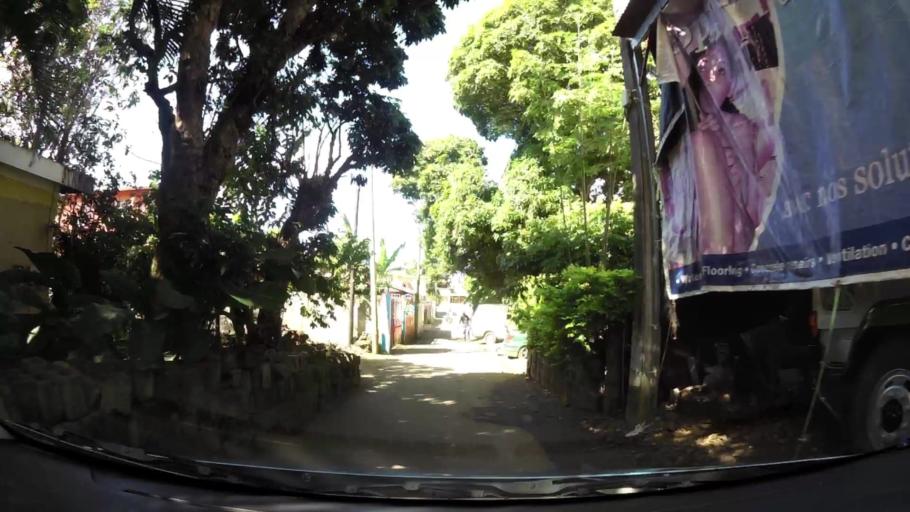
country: MU
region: Grand Port
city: Plaine Magnien
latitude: -20.4294
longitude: 57.6561
